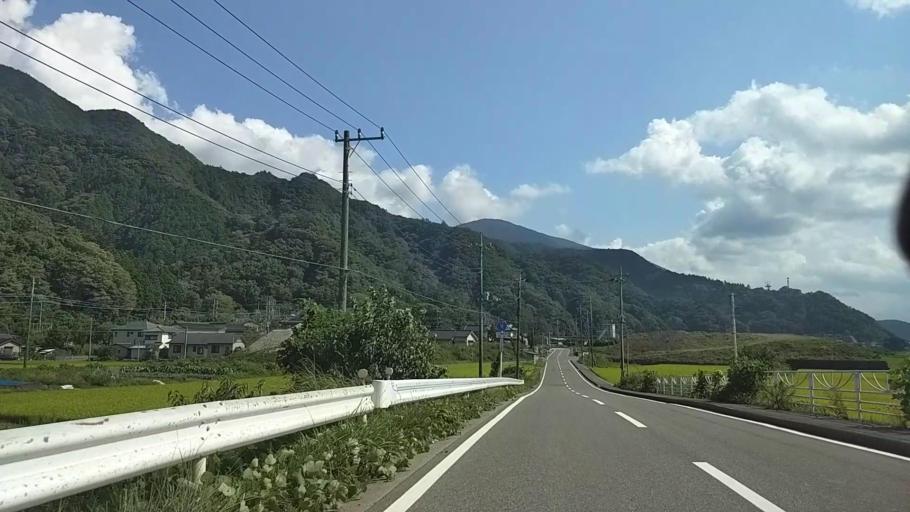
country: JP
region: Shizuoka
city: Fujinomiya
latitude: 35.3880
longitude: 138.4524
